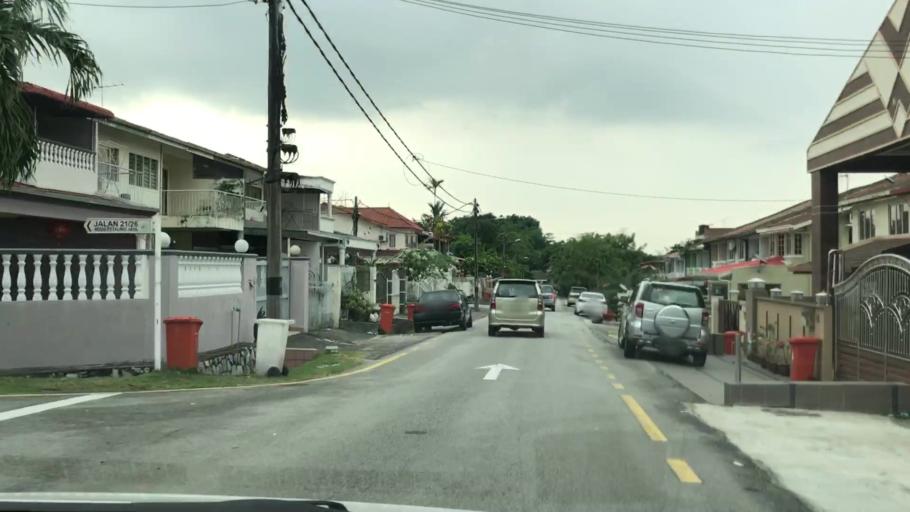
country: MY
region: Selangor
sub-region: Petaling
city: Petaling Jaya
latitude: 3.1096
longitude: 101.6197
